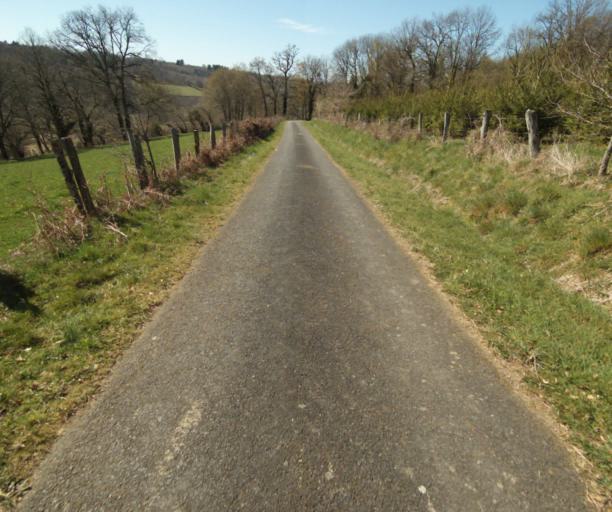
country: FR
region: Limousin
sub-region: Departement de la Correze
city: Chamboulive
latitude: 45.4448
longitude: 1.7079
